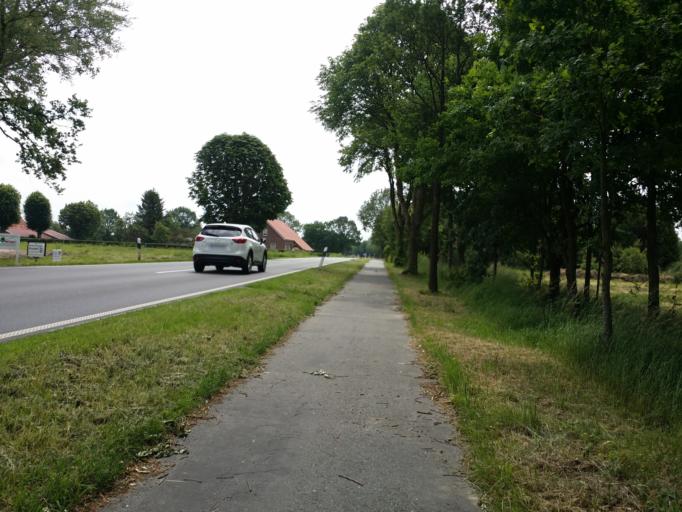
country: DE
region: Lower Saxony
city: Friedeburg
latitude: 53.4294
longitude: 7.8600
